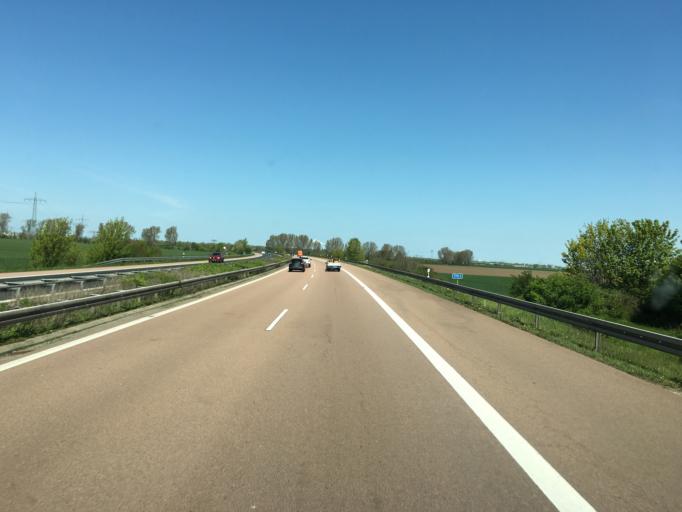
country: DE
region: Saxony-Anhalt
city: Beuna
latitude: 51.2901
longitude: 11.9756
